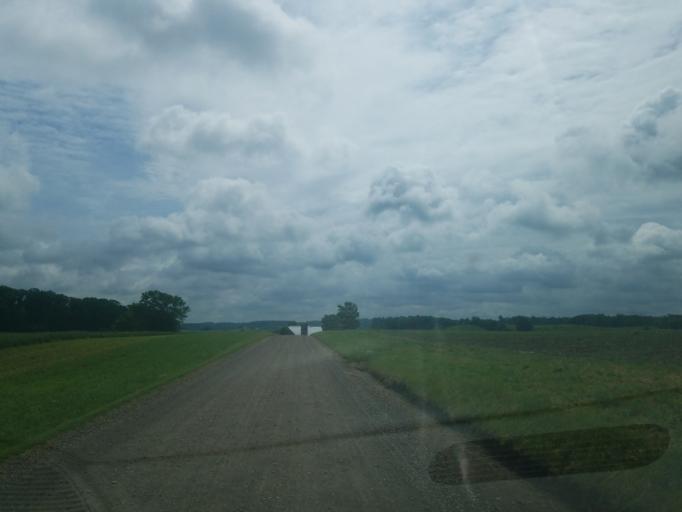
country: US
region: Ohio
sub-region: Tuscarawas County
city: Sugarcreek
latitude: 40.5156
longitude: -81.7641
